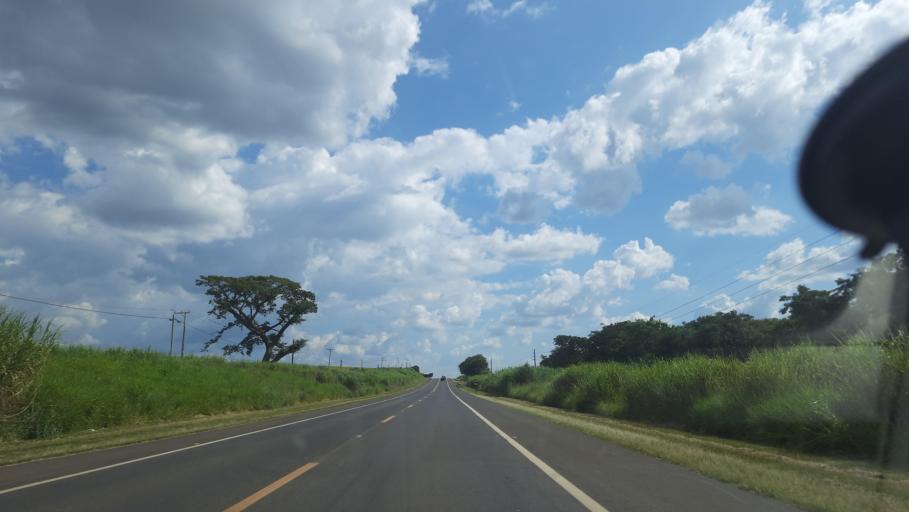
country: BR
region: Sao Paulo
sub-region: Sao Jose Do Rio Pardo
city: Sao Jose do Rio Pardo
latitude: -21.6713
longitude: -46.9225
